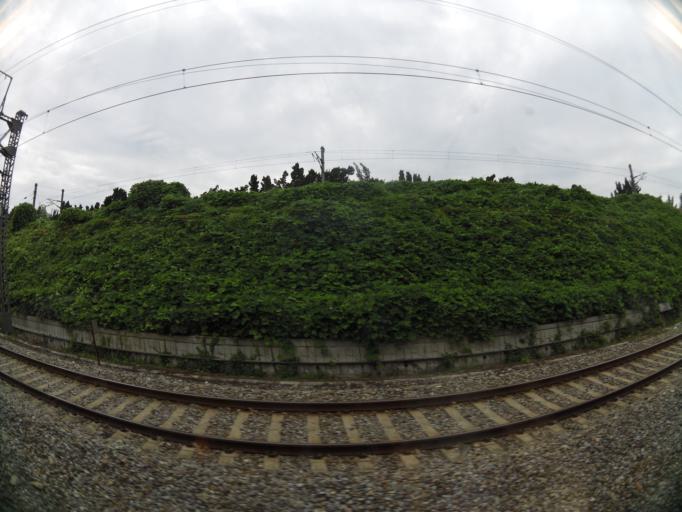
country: KR
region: Gyeonggi-do
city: Anyang-si
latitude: 37.3328
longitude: 126.9482
